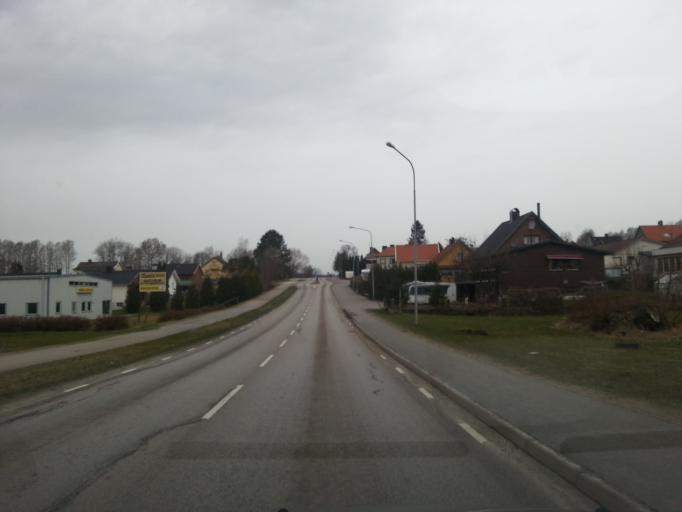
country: SE
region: Vaestra Goetaland
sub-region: Lilla Edets Kommun
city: Lilla Edet
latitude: 58.1296
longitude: 12.1300
